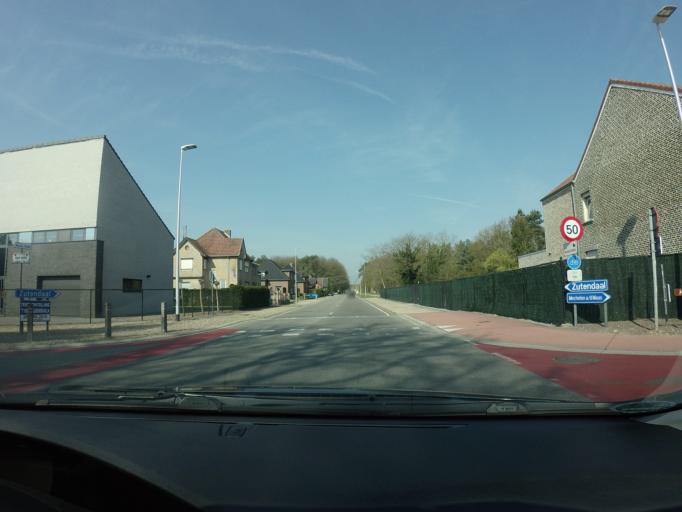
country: BE
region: Flanders
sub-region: Provincie Limburg
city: Maasmechelen
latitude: 50.9502
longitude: 5.6677
